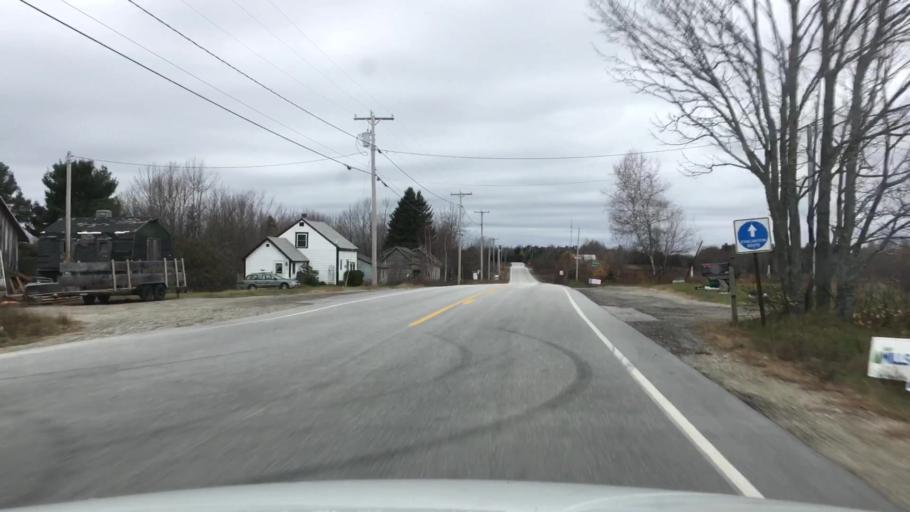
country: US
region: Maine
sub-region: Hancock County
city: Penobscot
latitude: 44.5221
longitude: -68.6612
